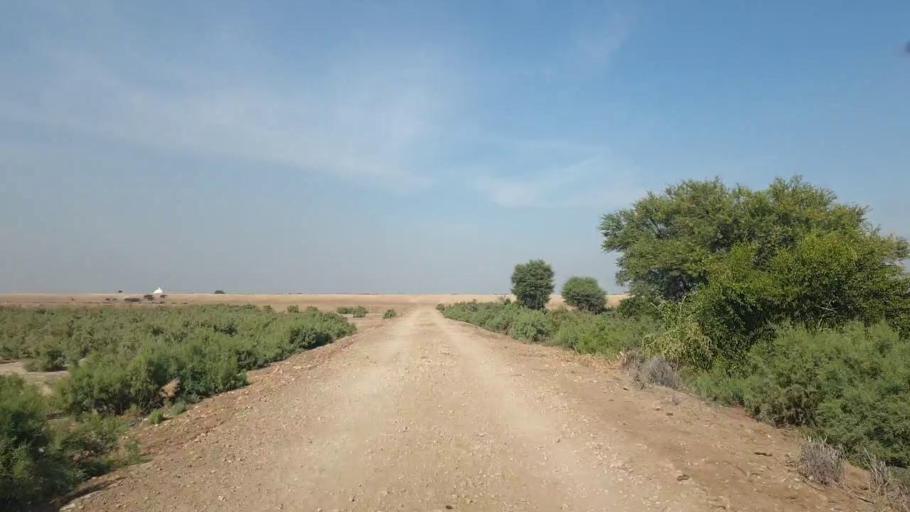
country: PK
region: Sindh
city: Sann
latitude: 25.9114
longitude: 68.2352
